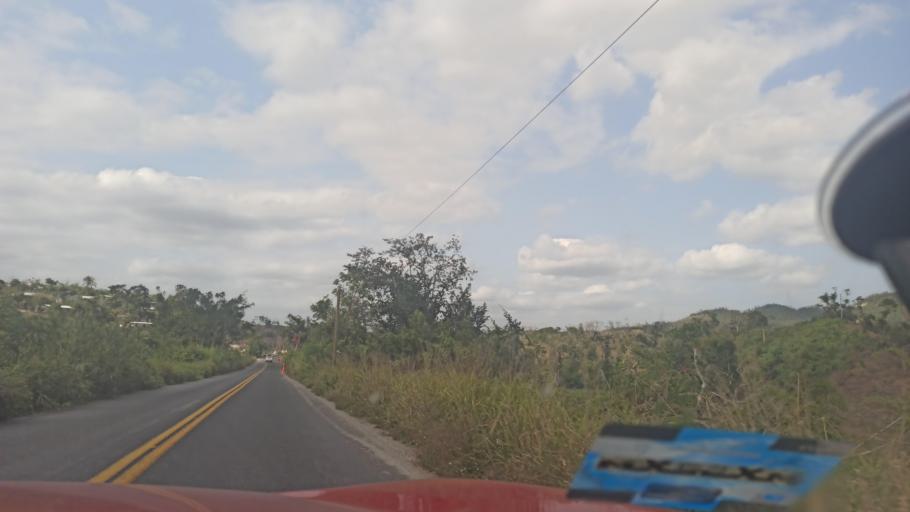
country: MX
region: Veracruz
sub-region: Papantla
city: Polutla
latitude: 20.4627
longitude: -97.2533
